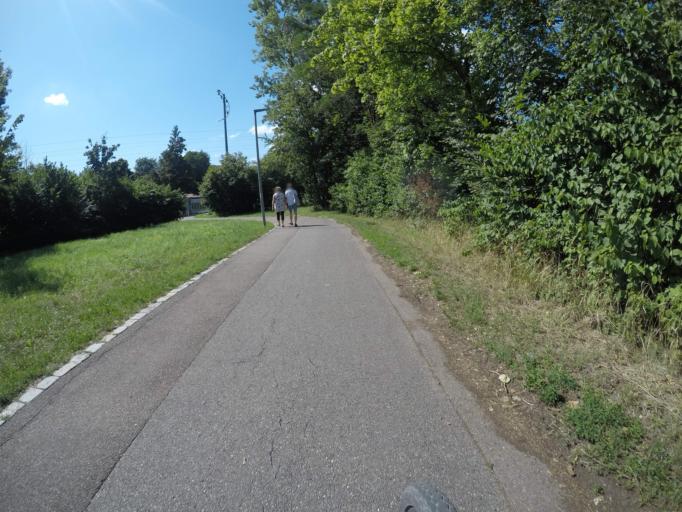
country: DE
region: Baden-Wuerttemberg
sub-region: Regierungsbezirk Stuttgart
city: Esslingen
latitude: 48.7274
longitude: 9.3251
